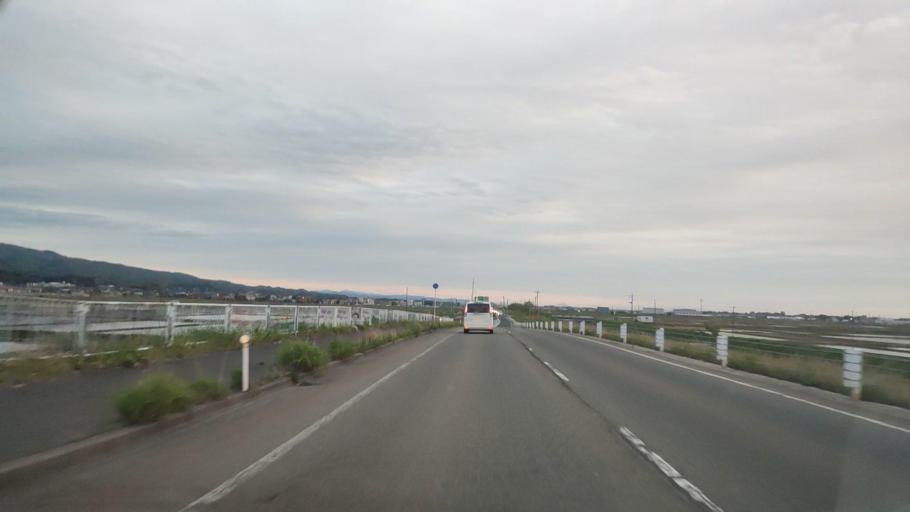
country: JP
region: Niigata
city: Niitsu-honcho
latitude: 37.7587
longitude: 139.0935
